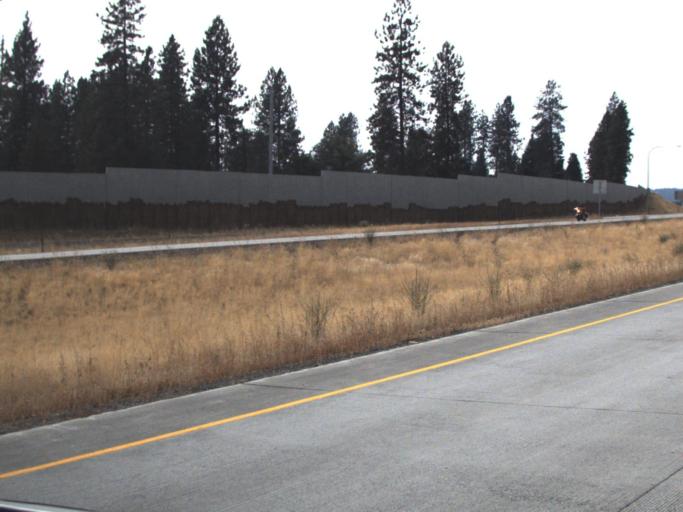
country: US
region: Washington
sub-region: Spokane County
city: Mead
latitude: 47.7784
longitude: -117.3786
